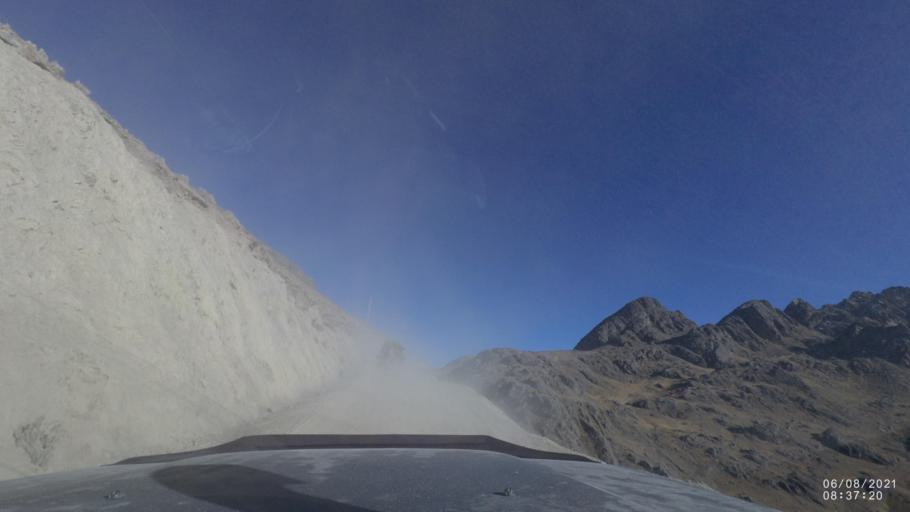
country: BO
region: Cochabamba
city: Sipe Sipe
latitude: -17.1756
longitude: -66.3885
